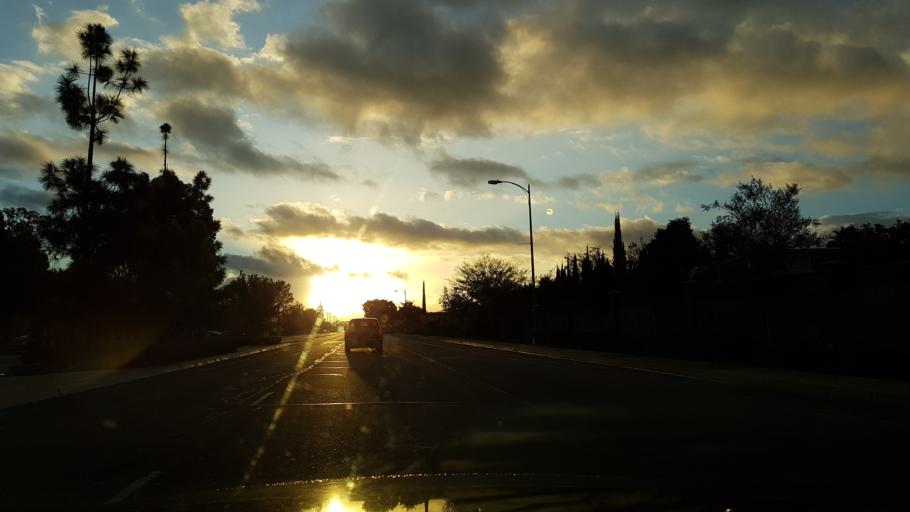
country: US
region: California
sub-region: San Diego County
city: Escondido
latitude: 33.1434
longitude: -117.0393
